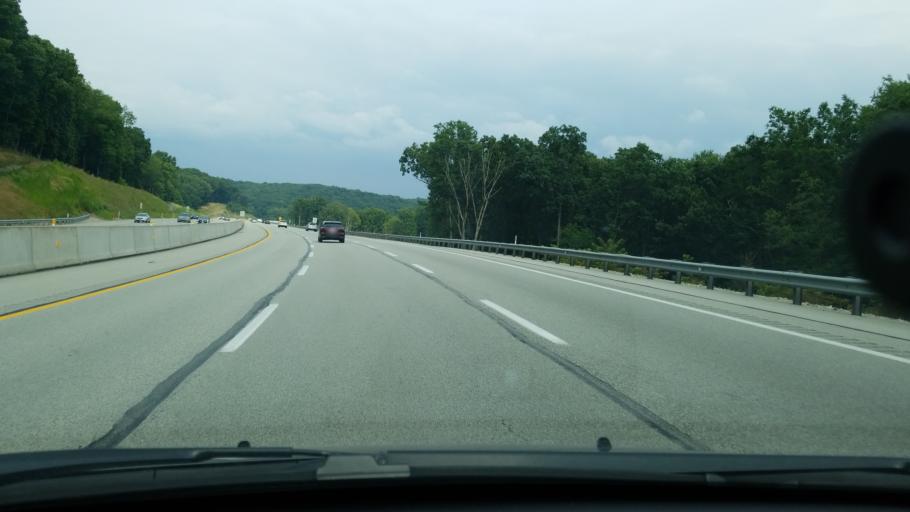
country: US
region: Pennsylvania
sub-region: Allegheny County
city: Gibsonia
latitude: 40.6399
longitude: -80.0069
